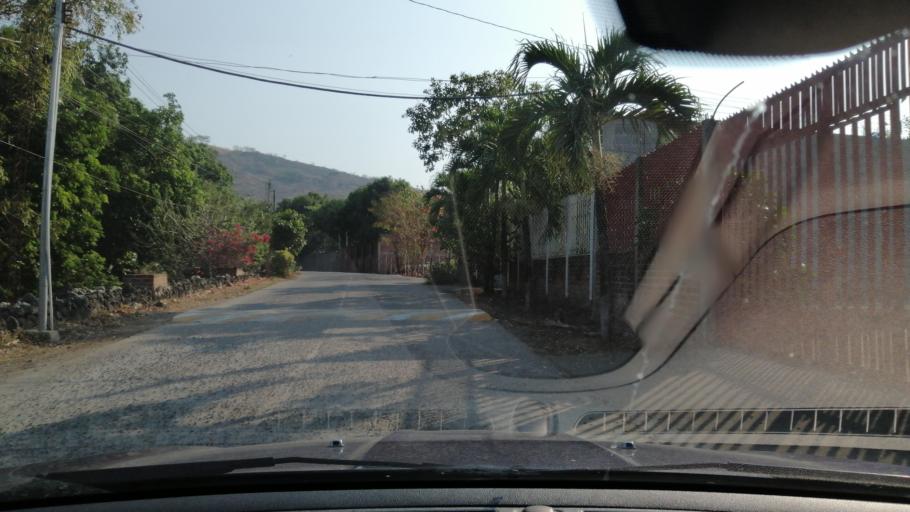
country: SV
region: Santa Ana
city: Texistepeque
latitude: 14.2196
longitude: -89.4585
